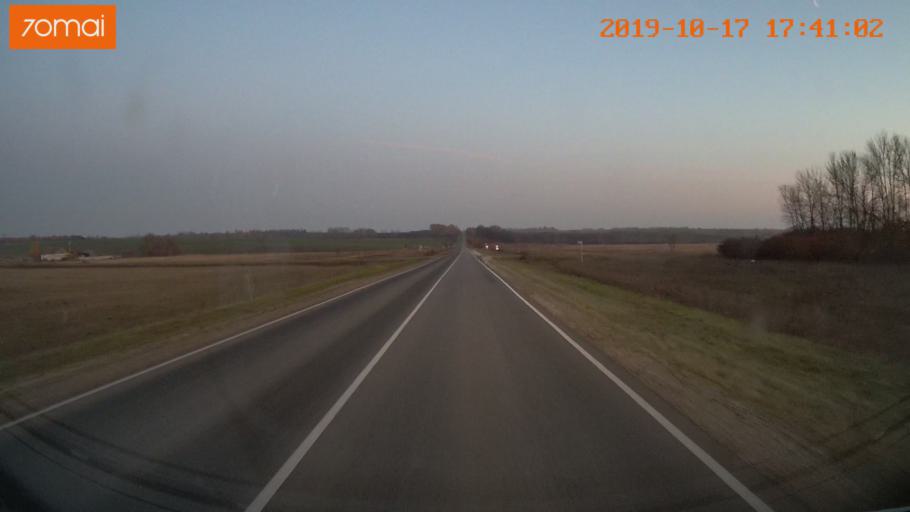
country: RU
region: Tula
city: Yepifan'
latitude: 53.7880
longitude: 38.6202
